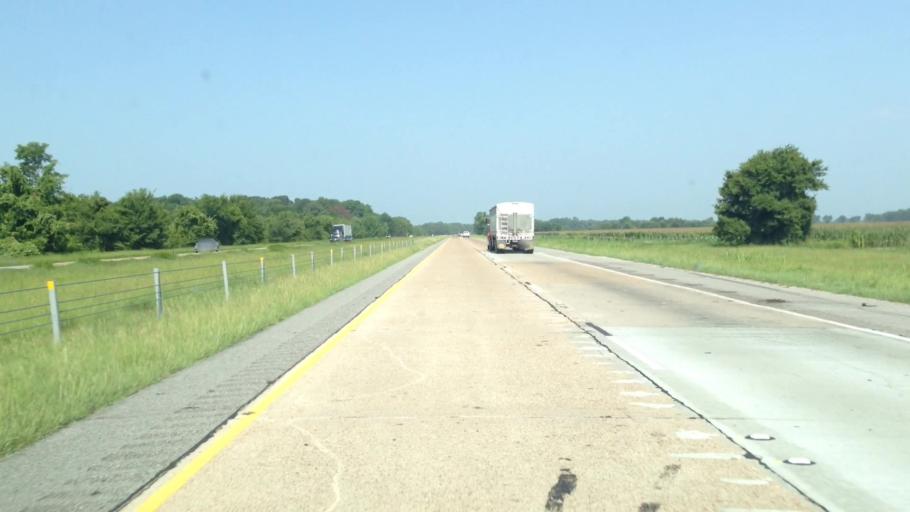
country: US
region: Mississippi
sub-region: Warren County
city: Vicksburg
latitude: 32.3327
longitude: -91.0409
